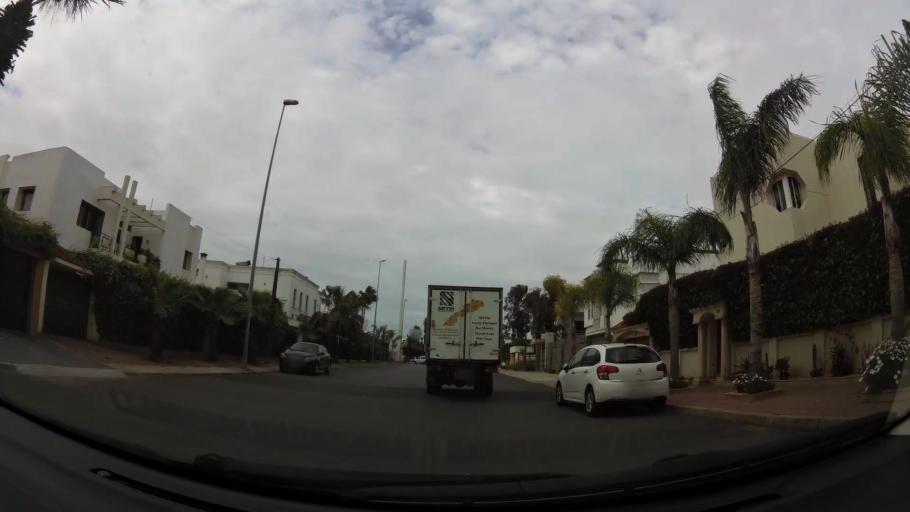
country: MA
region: Grand Casablanca
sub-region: Casablanca
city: Casablanca
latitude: 33.5722
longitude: -7.6624
